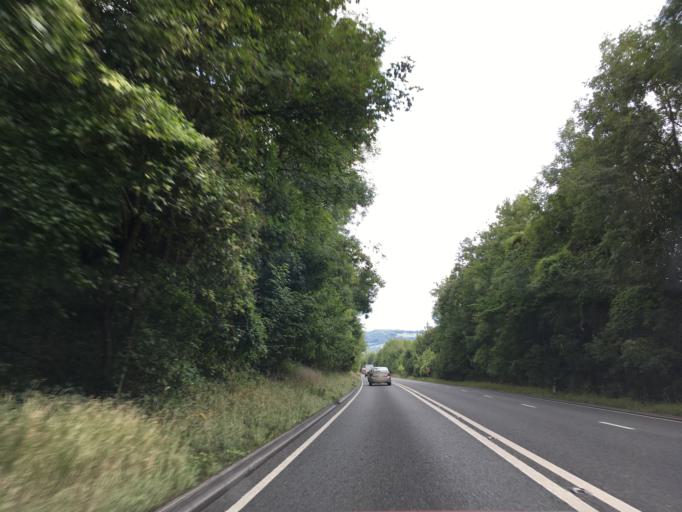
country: GB
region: England
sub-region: South Gloucestershire
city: Cold Ashton
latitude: 51.4206
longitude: -2.3531
